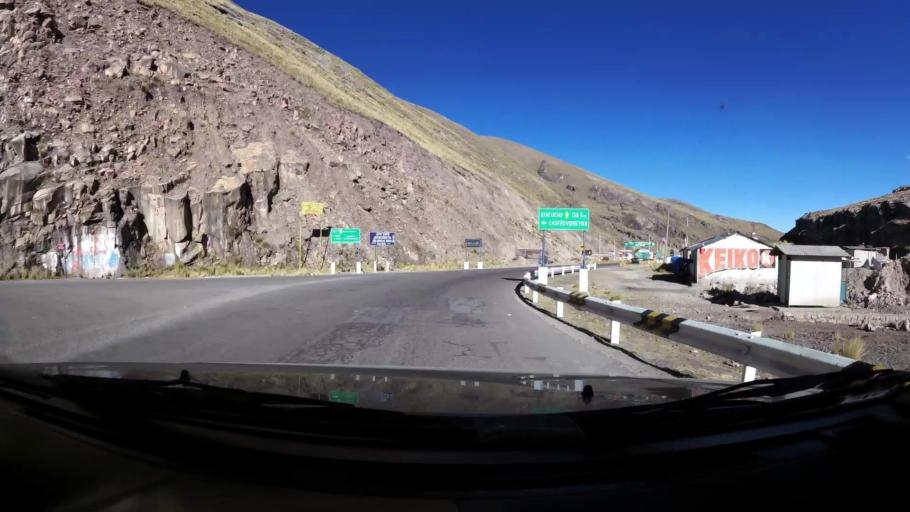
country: PE
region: Huancavelica
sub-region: Huaytara
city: Pilpichaca
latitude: -13.3736
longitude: -74.9403
